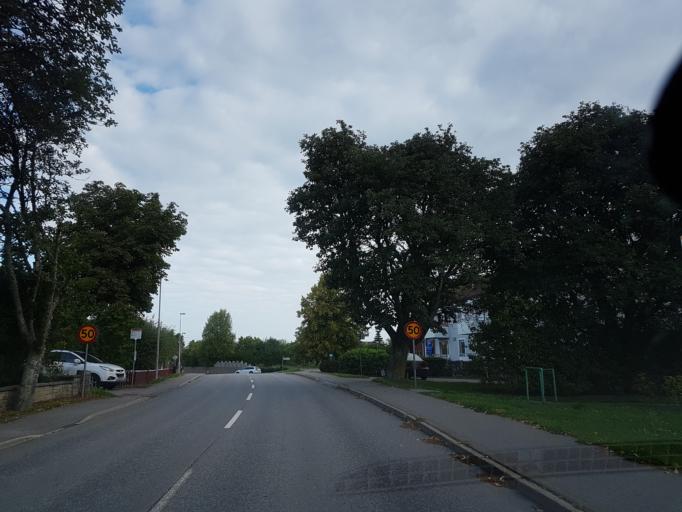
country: SE
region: OEstergoetland
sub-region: Linkopings Kommun
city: Vikingstad
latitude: 58.3828
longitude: 15.4363
